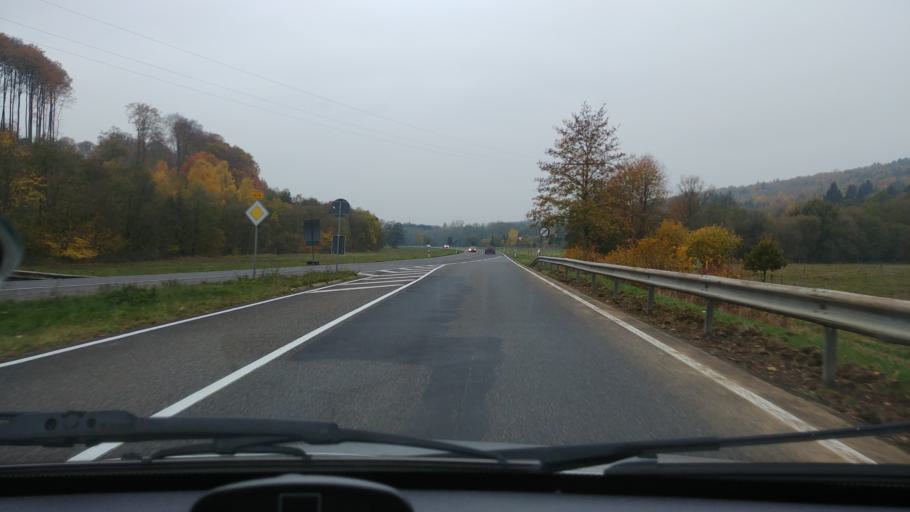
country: DE
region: Rheinland-Pfalz
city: Nister
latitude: 50.6720
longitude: 7.8598
